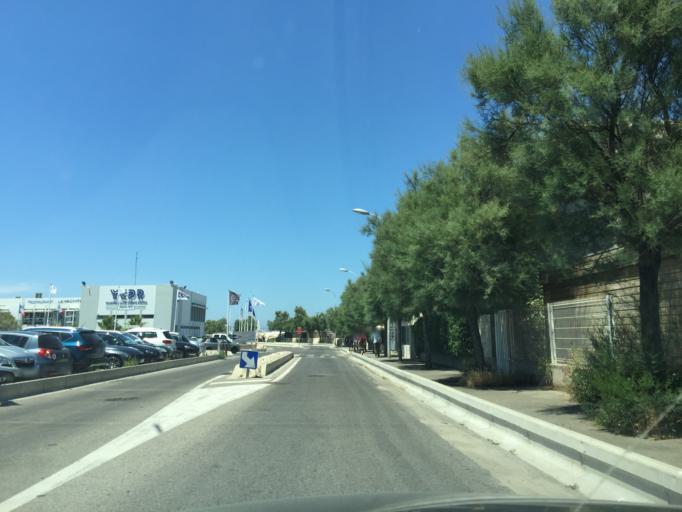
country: FR
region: Provence-Alpes-Cote d'Azur
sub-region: Departement des Bouches-du-Rhone
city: Marseille 08
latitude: 43.2442
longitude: 5.3690
